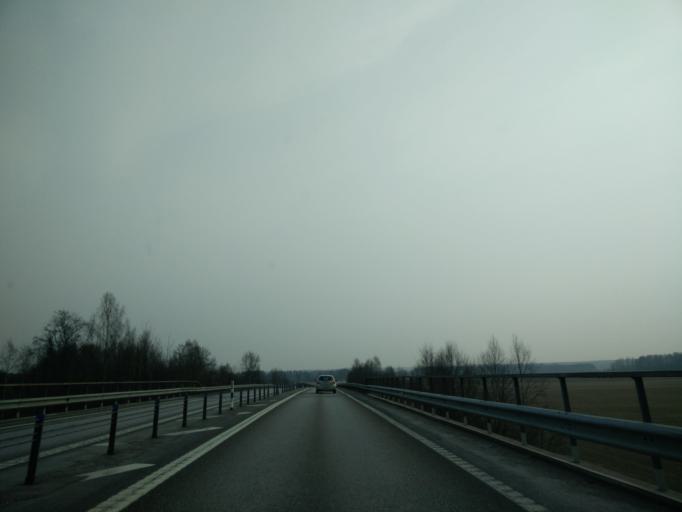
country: SE
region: Vaermland
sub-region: Forshaga Kommun
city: Forshaga
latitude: 59.4433
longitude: 13.4161
